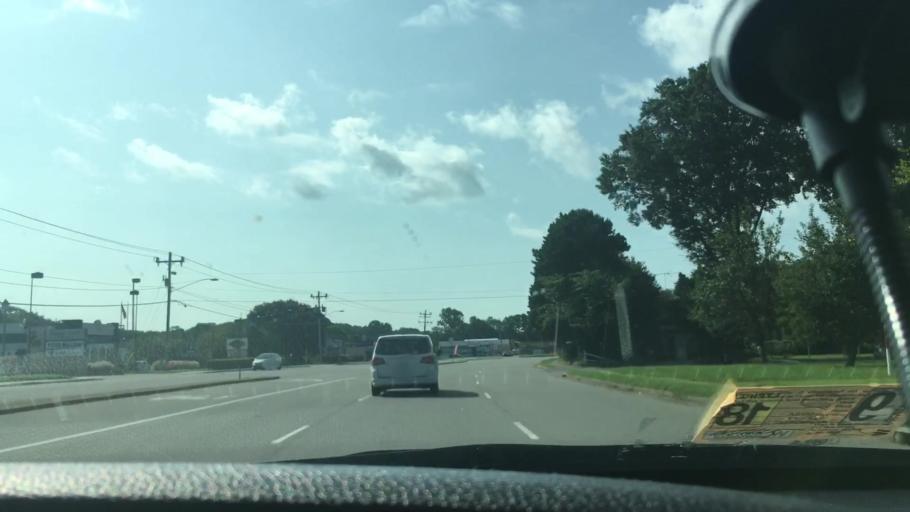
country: US
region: Virginia
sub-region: City of Virginia Beach
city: Virginia Beach
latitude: 36.8773
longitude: -76.0409
